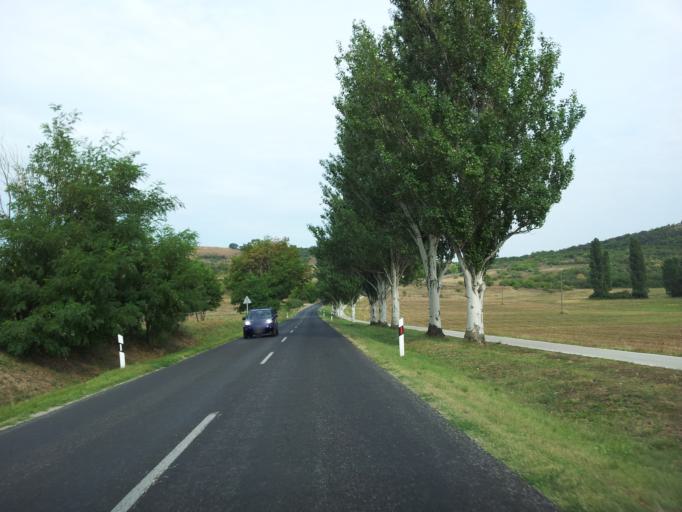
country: HU
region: Veszprem
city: Tihany
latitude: 46.9196
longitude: 17.8662
